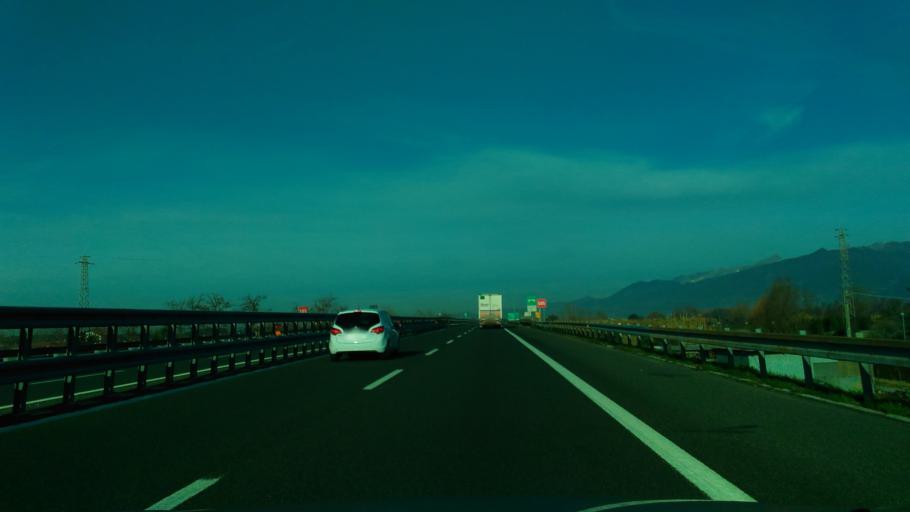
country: IT
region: Tuscany
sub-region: Provincia di Lucca
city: Camaiore
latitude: 43.9207
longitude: 10.2301
